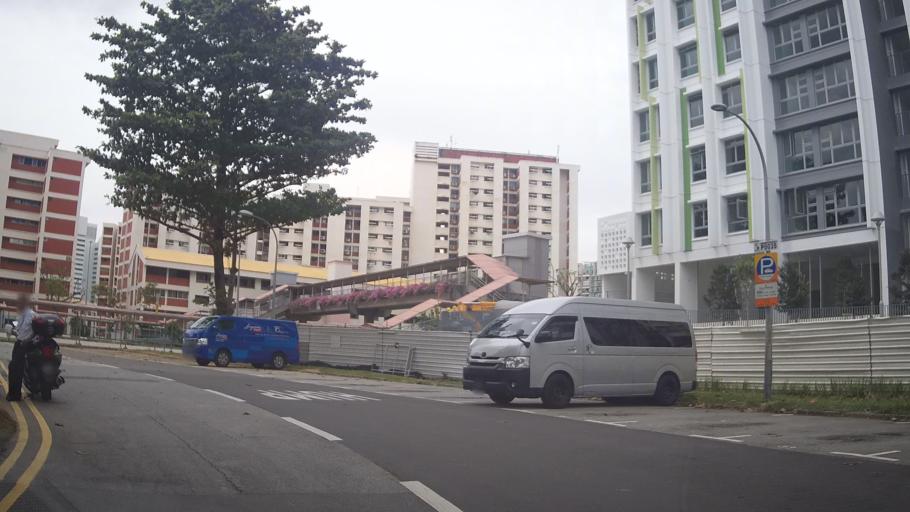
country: SG
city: Singapore
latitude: 1.3331
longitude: 103.8702
